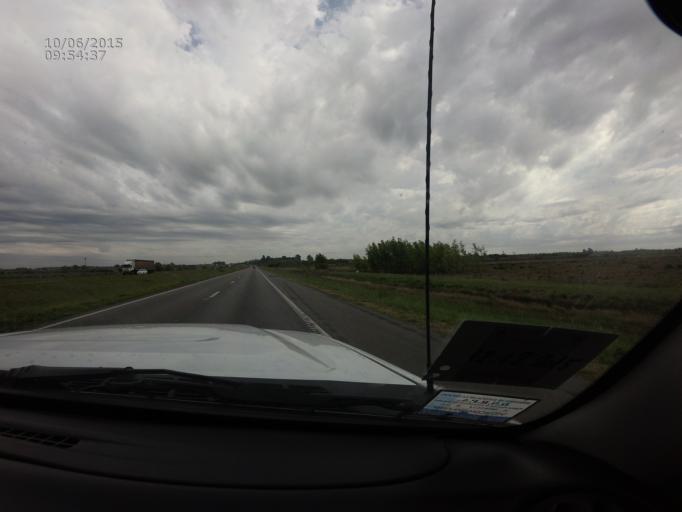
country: AR
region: Buenos Aires
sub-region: Partido de Baradero
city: Baradero
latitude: -33.9568
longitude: -59.3959
